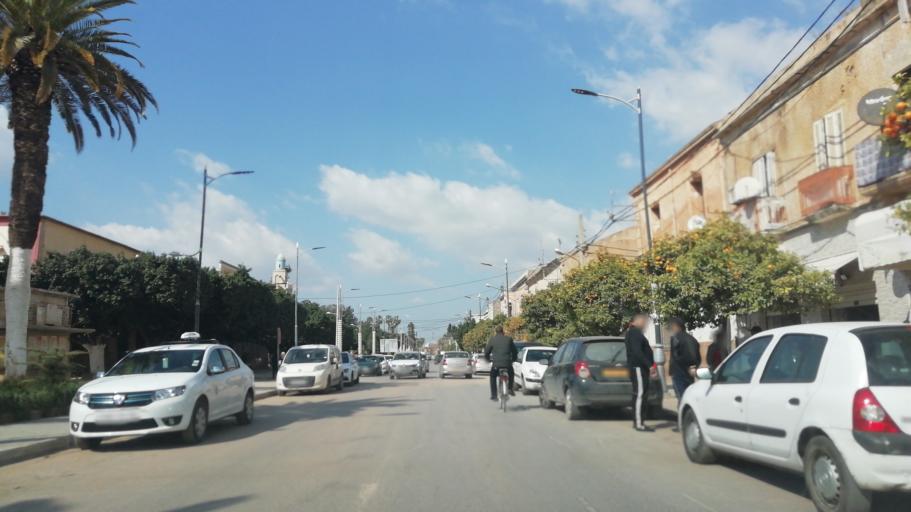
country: DZ
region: Mascara
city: Mascara
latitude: 35.5893
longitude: 0.0667
